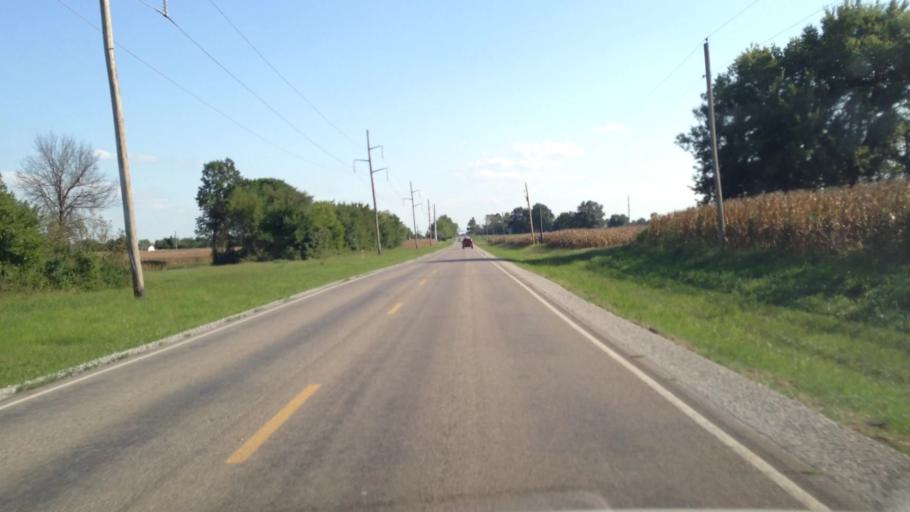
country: US
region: Kansas
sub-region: Crawford County
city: Pittsburg
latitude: 37.3717
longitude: -94.6314
